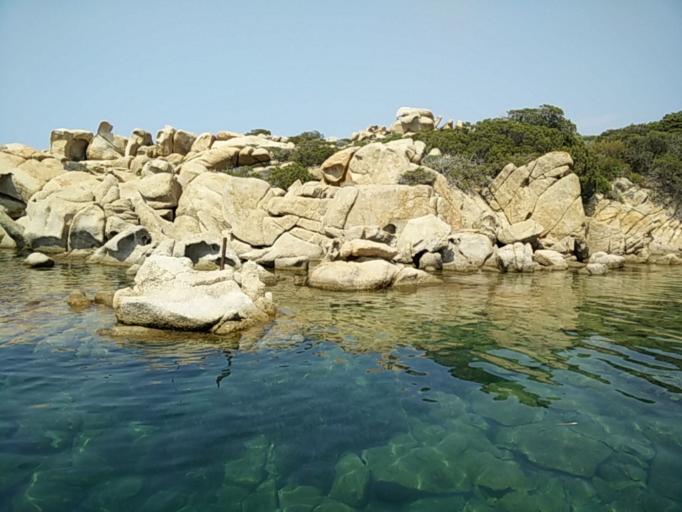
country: FR
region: Corsica
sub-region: Departement de la Corse-du-Sud
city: Propriano
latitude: 41.5641
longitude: 8.7889
